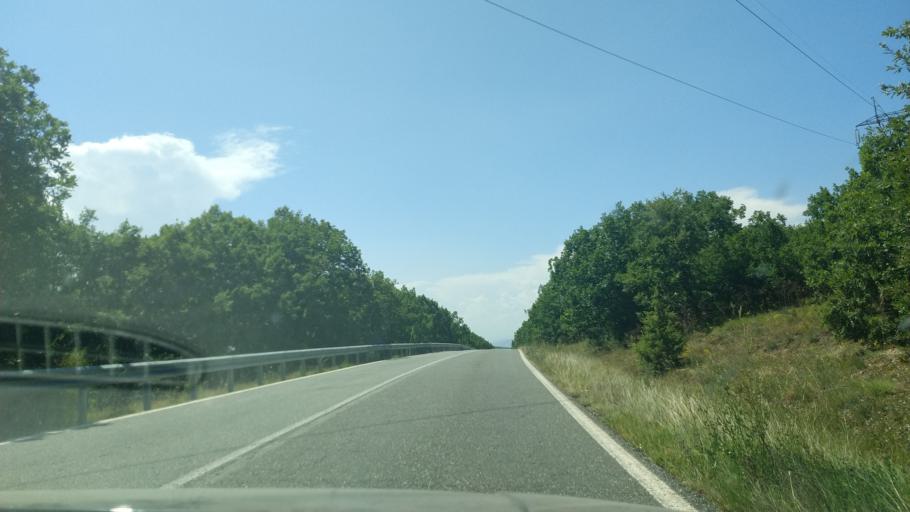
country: GR
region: West Macedonia
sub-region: Nomos Grevenon
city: Grevena
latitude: 39.9973
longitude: 21.5005
